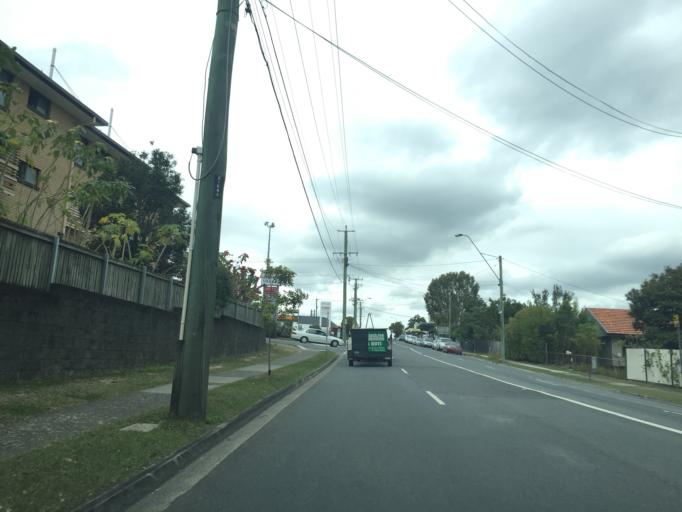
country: AU
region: Queensland
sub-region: Brisbane
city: Milton
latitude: -27.4435
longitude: 152.9910
